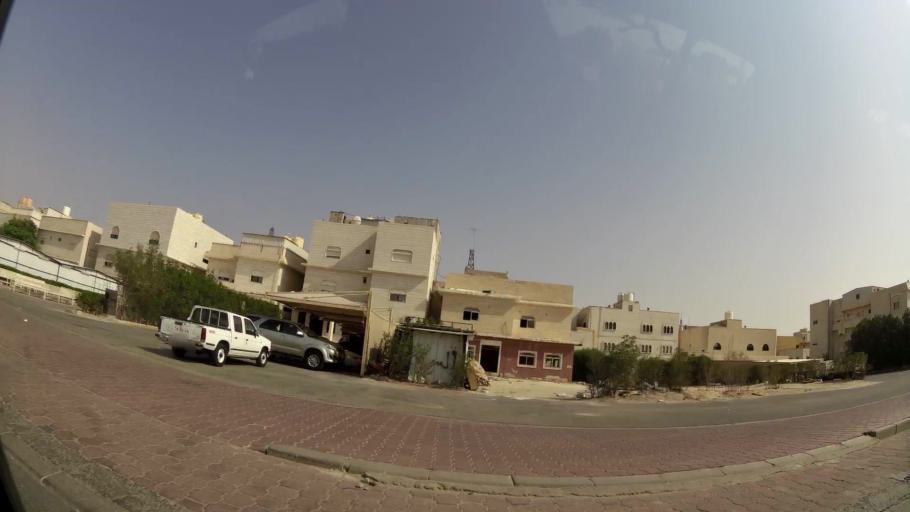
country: KW
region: Muhafazat al Jahra'
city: Al Jahra'
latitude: 29.3340
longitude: 47.6487
